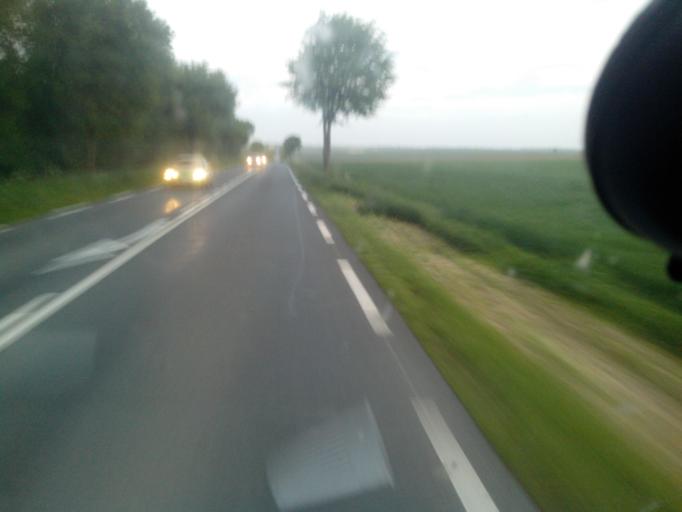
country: FR
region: Nord-Pas-de-Calais
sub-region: Departement du Pas-de-Calais
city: Auchy-les-Hesdin
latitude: 50.4229
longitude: 2.0577
